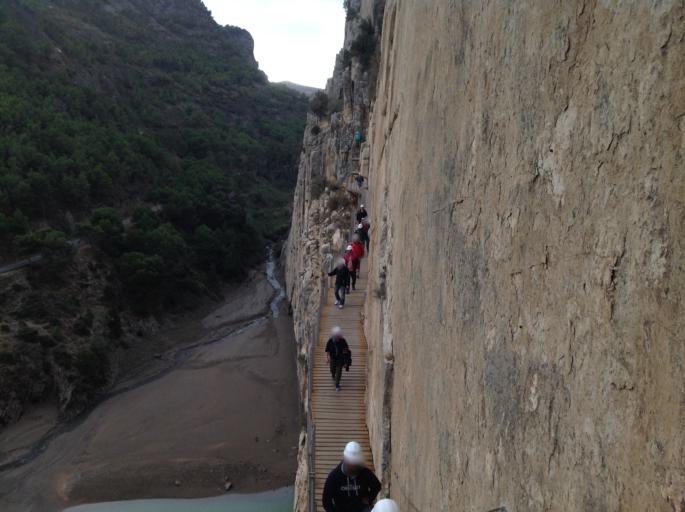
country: ES
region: Andalusia
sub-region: Provincia de Malaga
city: Carratraca
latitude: 36.9159
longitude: -4.7710
